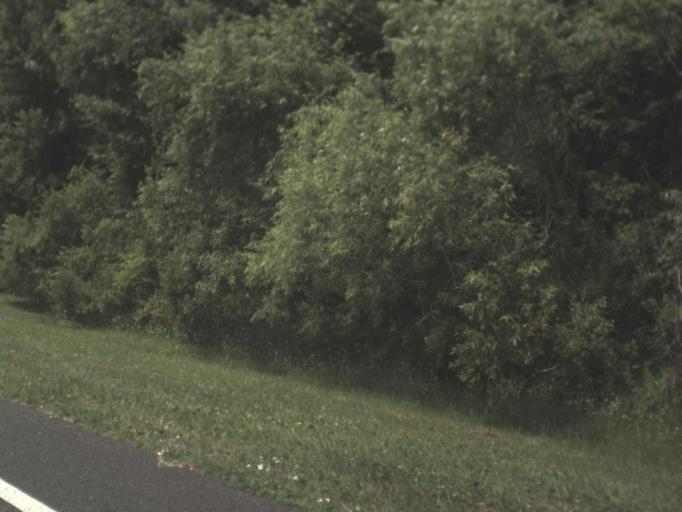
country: US
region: Florida
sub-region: Clay County
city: Green Cove Springs
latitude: 29.8492
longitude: -81.6625
